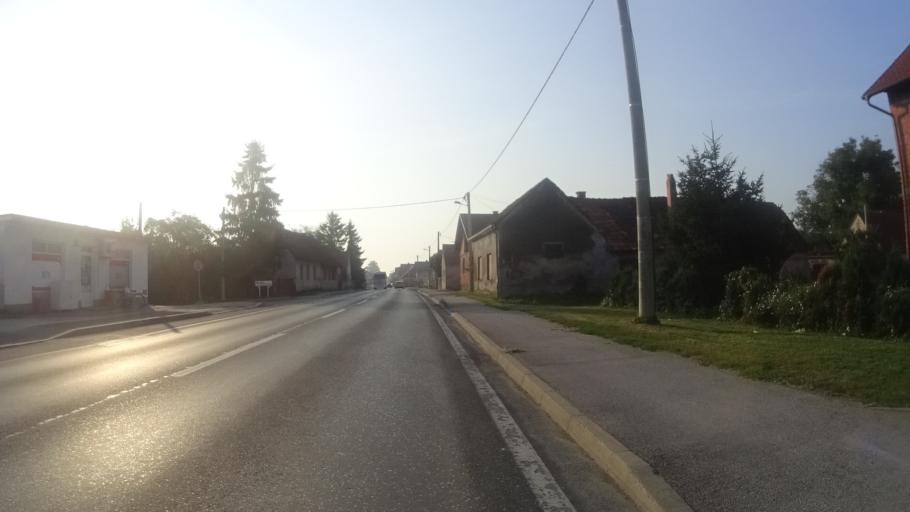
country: HR
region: Varazdinska
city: Petrijanec
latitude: 46.3459
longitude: 16.2272
